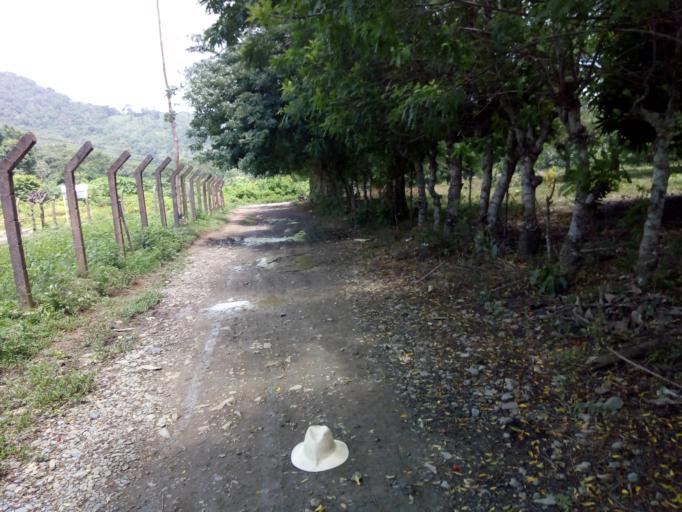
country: PA
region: Guna Yala
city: Puerto Obaldia
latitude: 8.6291
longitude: -77.3527
